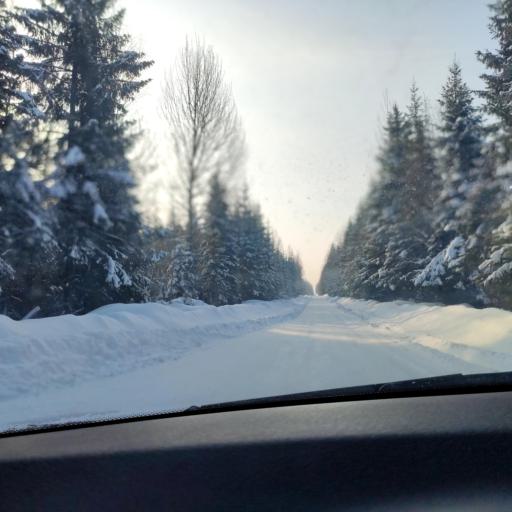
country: RU
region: Perm
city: Kondratovo
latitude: 58.0750
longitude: 56.1291
